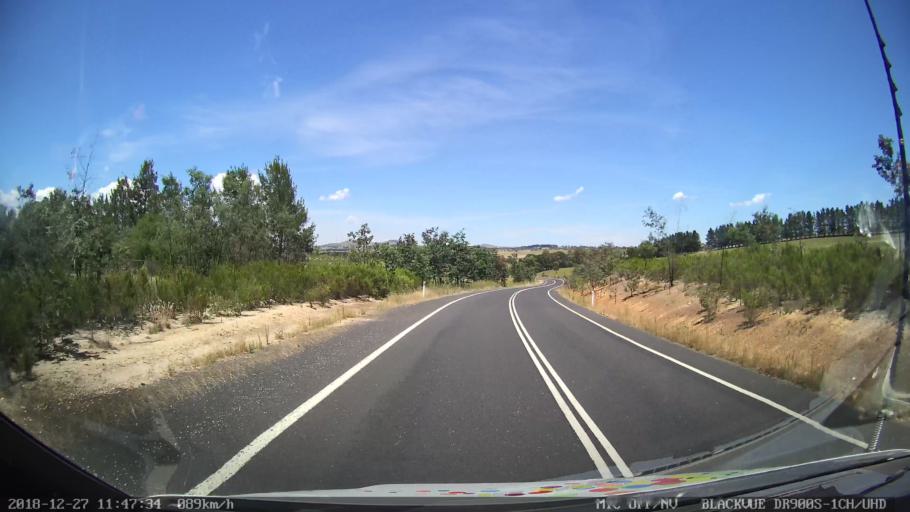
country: AU
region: New South Wales
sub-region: Bathurst Regional
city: Perthville
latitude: -33.5977
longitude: 149.4436
